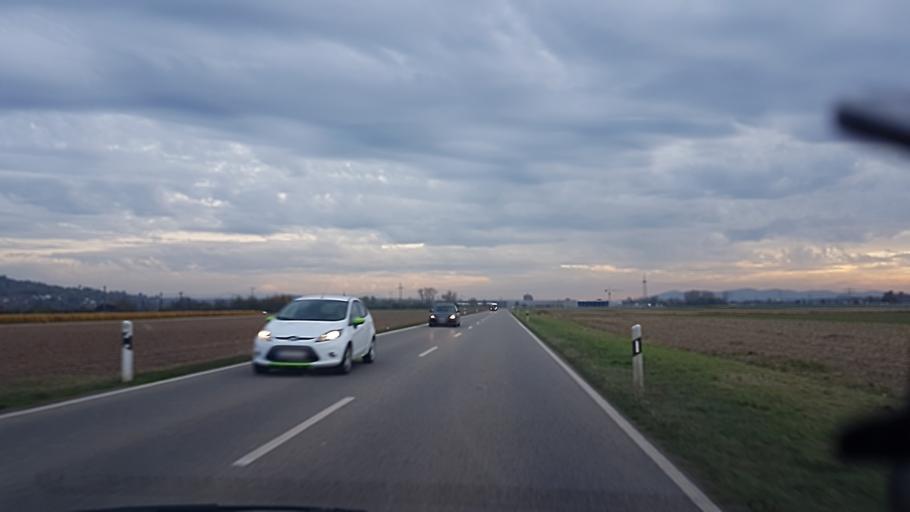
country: DE
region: Baden-Wuerttemberg
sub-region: Freiburg Region
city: Ringsheim
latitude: 48.2407
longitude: 7.7675
